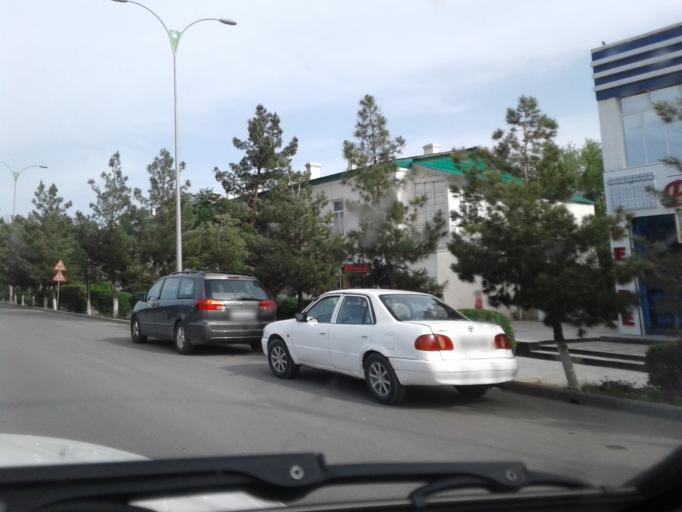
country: TM
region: Mary
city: Mary
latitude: 37.5907
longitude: 61.8302
